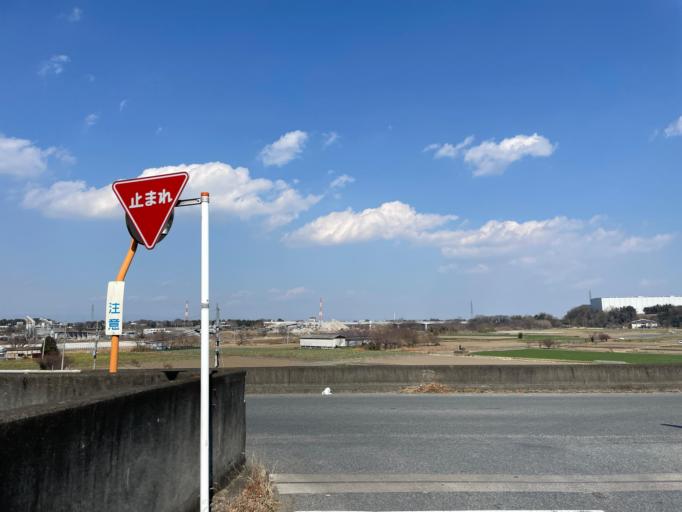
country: JP
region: Saitama
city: Yorii
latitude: 36.1143
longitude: 139.2438
